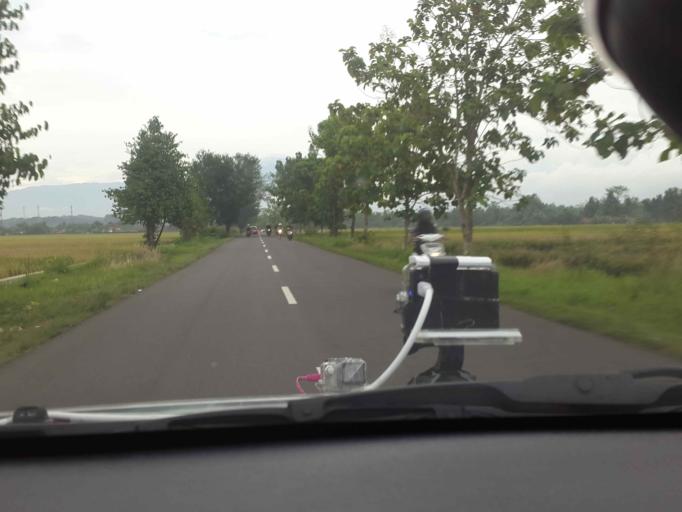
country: ID
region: Central Java
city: Banyumas
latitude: -7.5264
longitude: 109.3043
